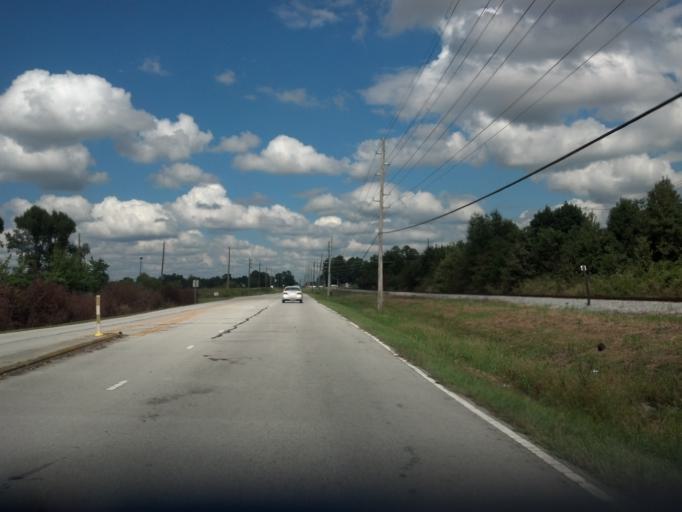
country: US
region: North Carolina
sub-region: Pitt County
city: Winterville
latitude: 35.5153
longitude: -77.4076
